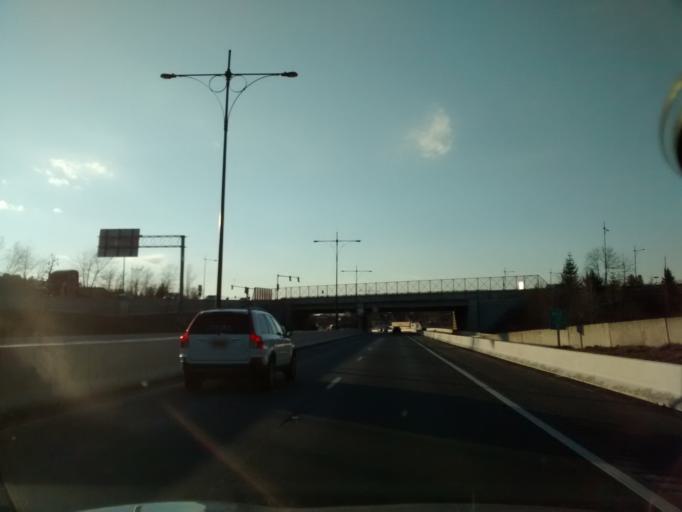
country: US
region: Massachusetts
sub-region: Worcester County
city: Sunderland
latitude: 42.2354
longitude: -71.7921
